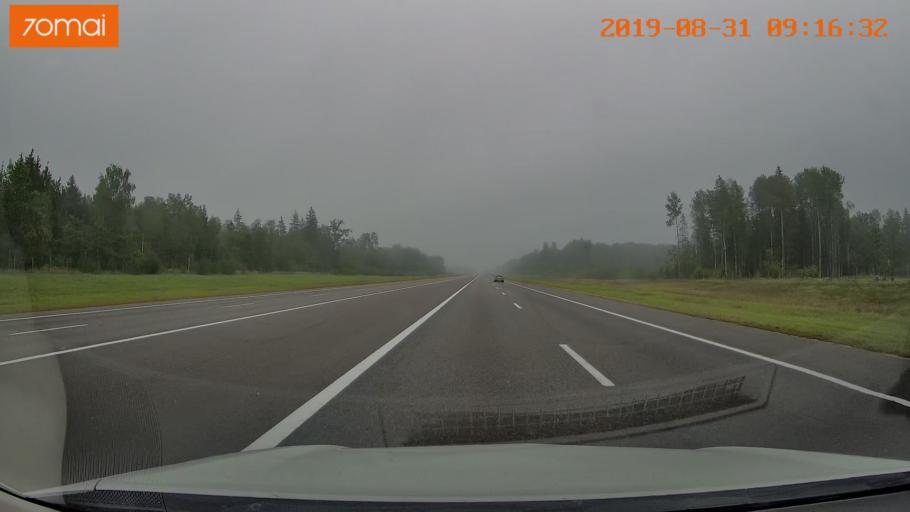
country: BY
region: Minsk
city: Byerazino
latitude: 53.7716
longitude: 28.7131
